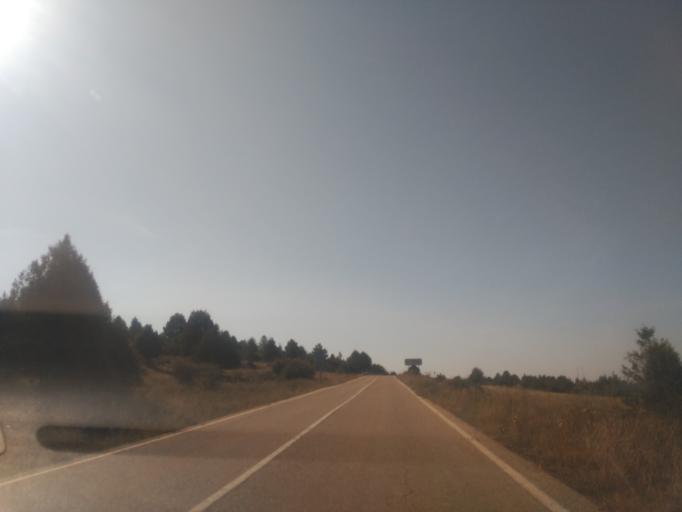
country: ES
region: Castille and Leon
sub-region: Provincia de Soria
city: Casarejos
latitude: 41.7782
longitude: -3.0267
